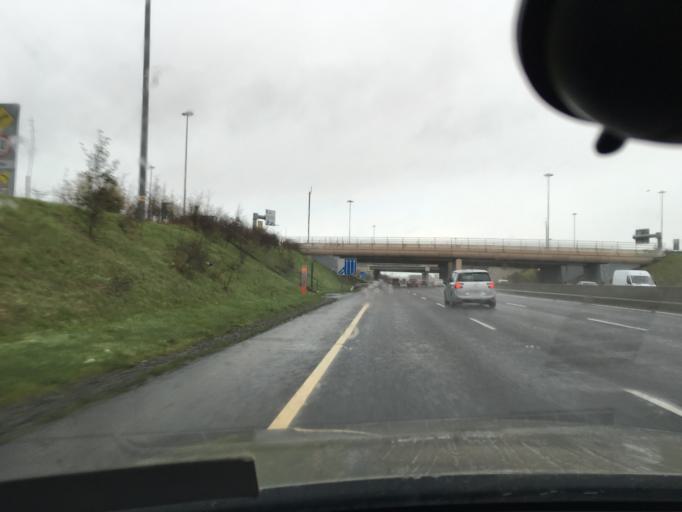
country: IE
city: Cherry Orchard
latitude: 53.3166
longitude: -6.3670
